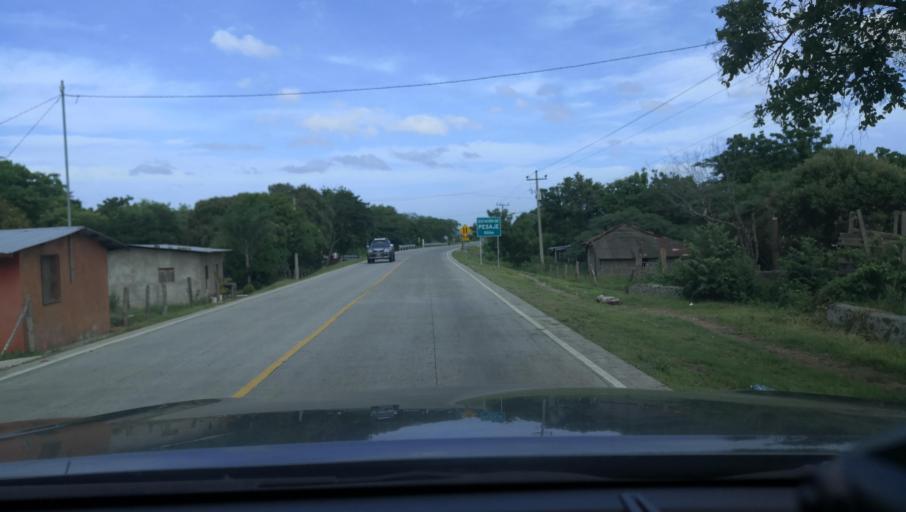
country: NI
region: Boaco
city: San Lorenzo
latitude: 12.1888
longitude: -85.7097
